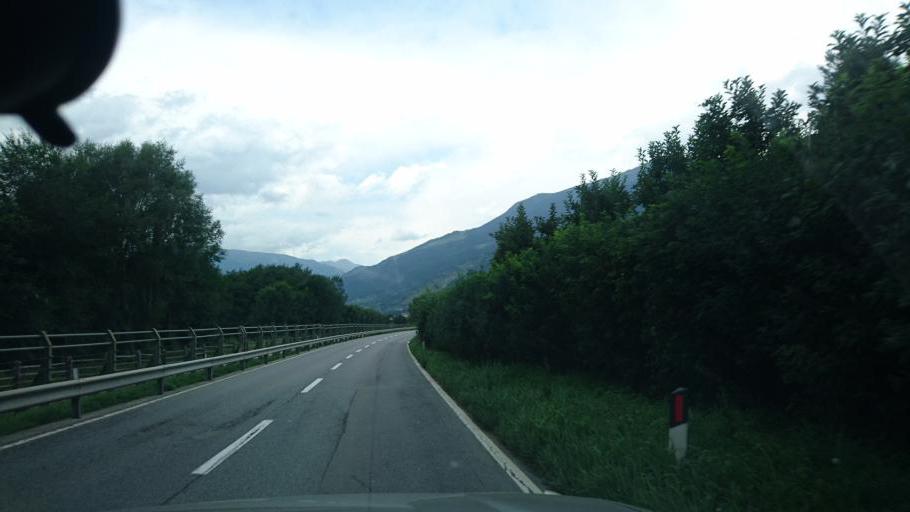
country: IT
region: Trentino-Alto Adige
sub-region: Bolzano
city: Sluderno
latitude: 46.6514
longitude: 10.5904
